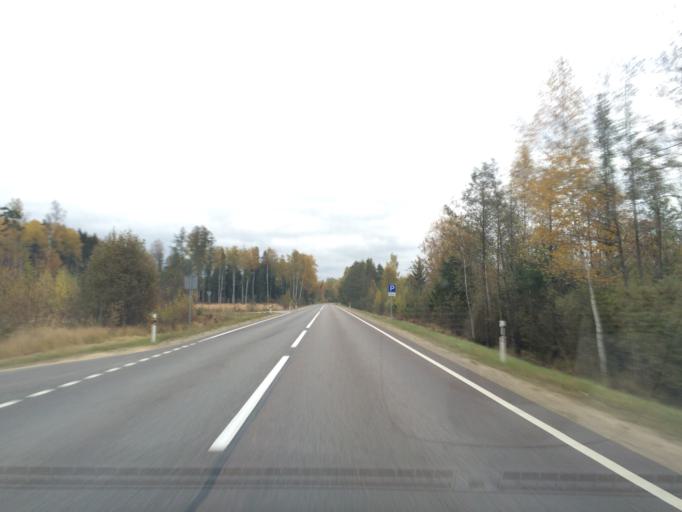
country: LV
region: Livani
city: Livani
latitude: 56.5270
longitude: 26.1943
